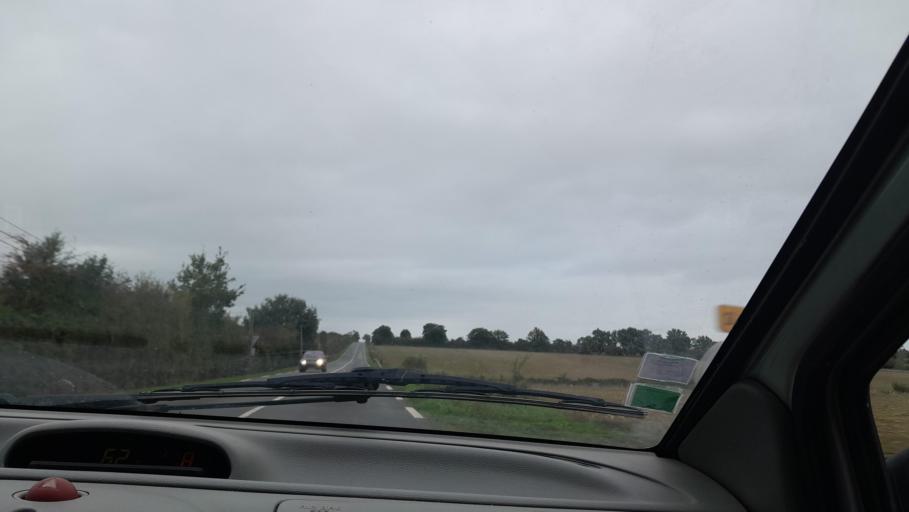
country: FR
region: Pays de la Loire
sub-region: Departement de la Loire-Atlantique
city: Saint-Mars-la-Jaille
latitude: 47.6279
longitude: -1.2001
